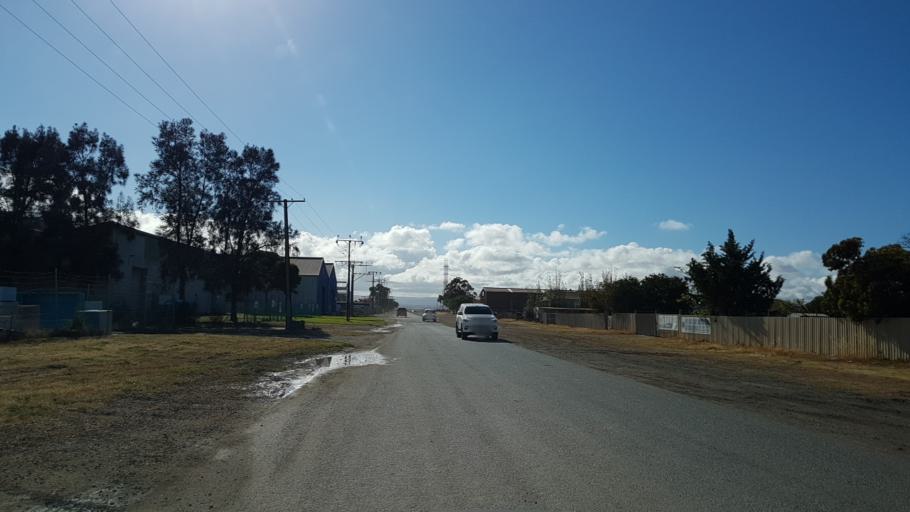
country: AU
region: South Australia
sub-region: Port Adelaide Enfield
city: Birkenhead
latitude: -34.8130
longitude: 138.5189
